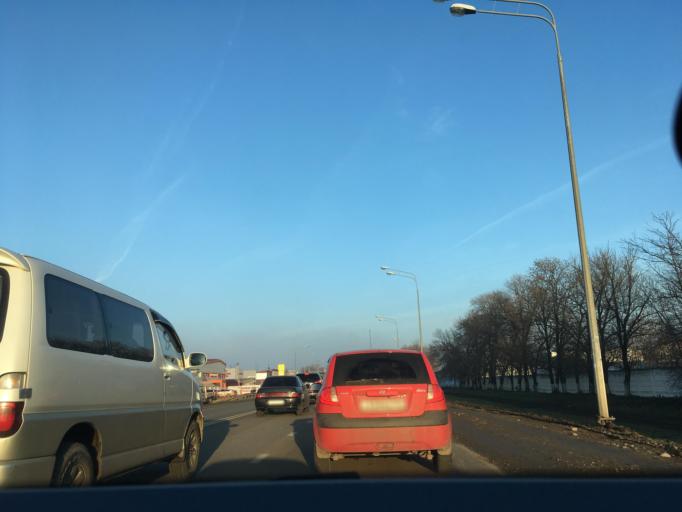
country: RU
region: Krasnodarskiy
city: Krasnodar
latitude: 45.1318
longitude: 39.0213
